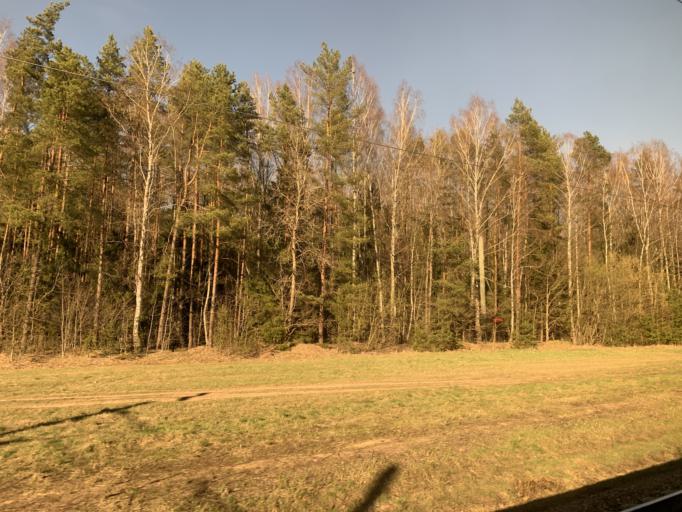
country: BY
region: Grodnenskaya
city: Smarhon'
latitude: 54.4902
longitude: 26.2974
